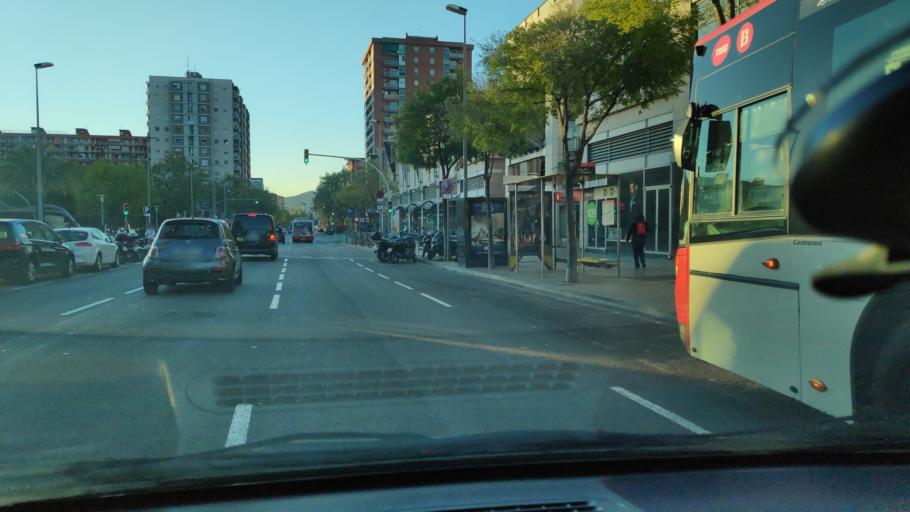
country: ES
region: Catalonia
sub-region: Provincia de Barcelona
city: Sant Marti
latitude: 41.4091
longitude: 2.2155
